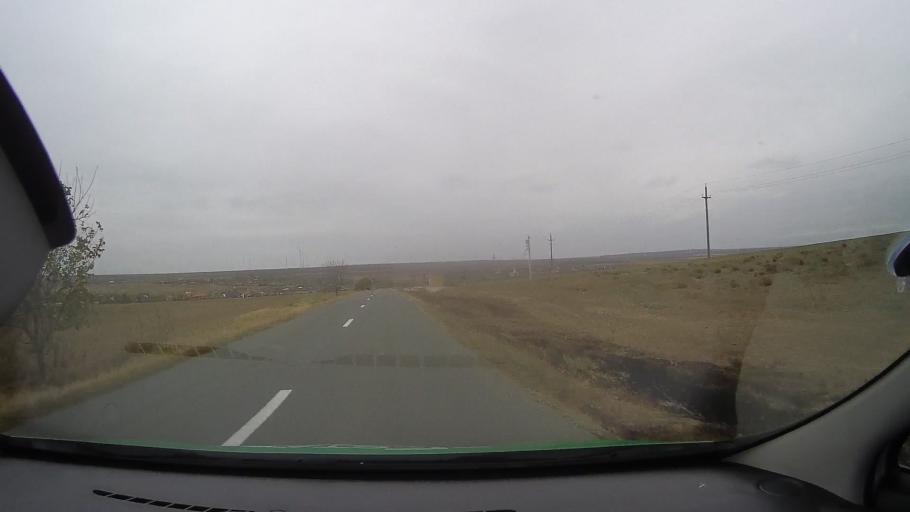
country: RO
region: Constanta
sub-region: Comuna Targusor
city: Targusor
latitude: 44.4869
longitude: 28.3660
